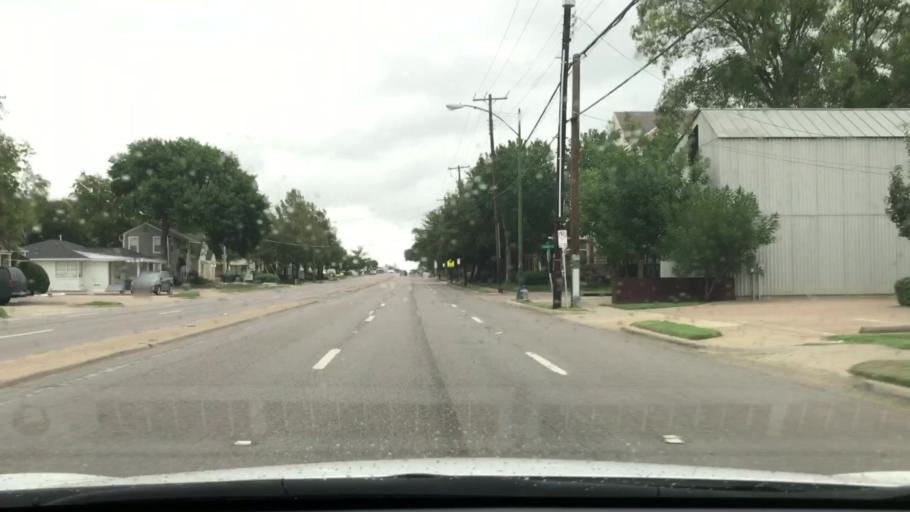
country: US
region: Texas
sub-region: Dallas County
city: University Park
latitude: 32.8512
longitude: -96.8292
